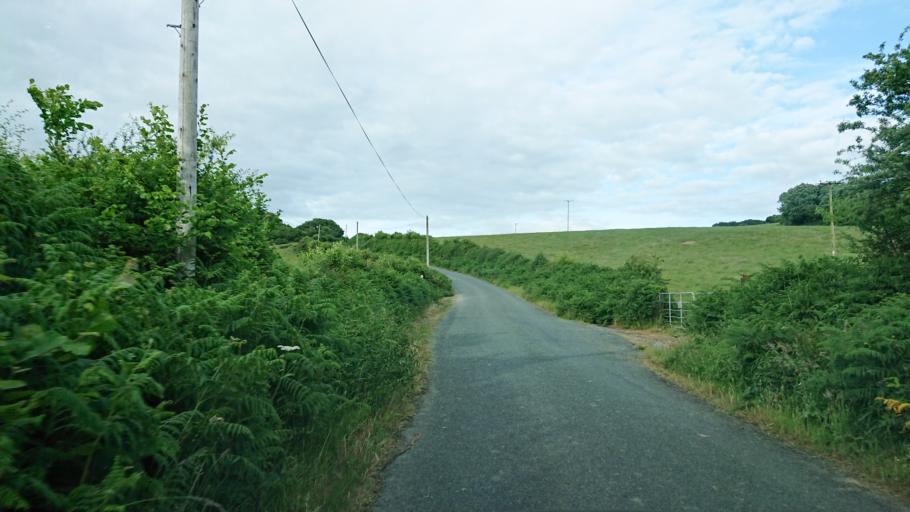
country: IE
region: Munster
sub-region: Waterford
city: Tra Mhor
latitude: 52.2045
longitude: -7.2196
